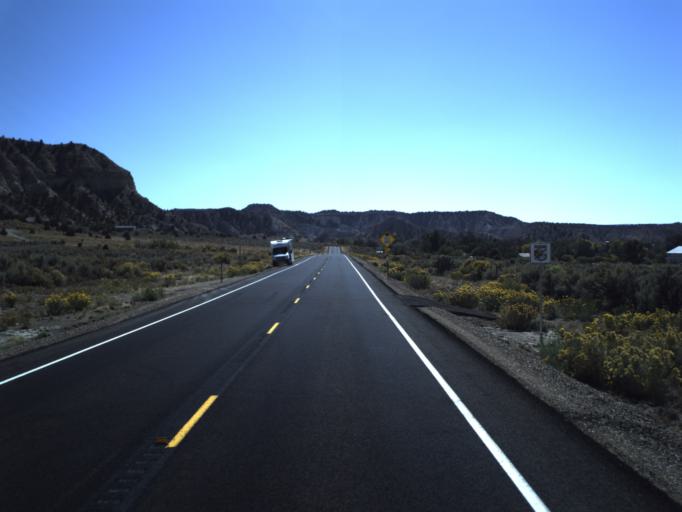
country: US
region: Utah
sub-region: Garfield County
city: Panguitch
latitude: 37.5704
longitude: -111.9891
